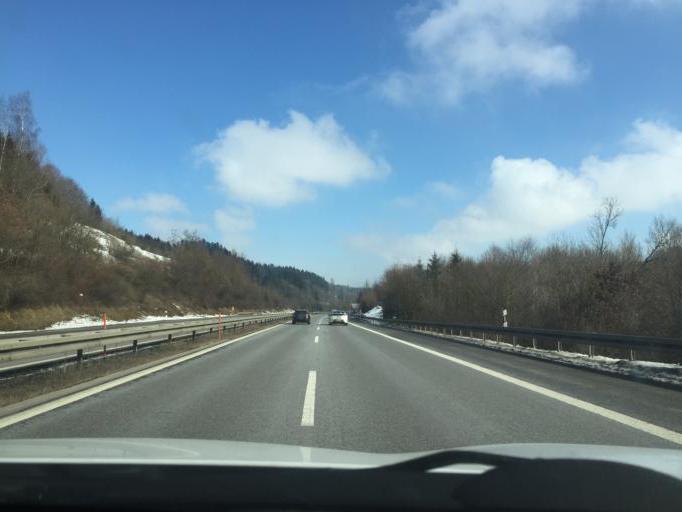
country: DE
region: Baden-Wuerttemberg
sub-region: Tuebingen Region
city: Wangen im Allgau
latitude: 47.7166
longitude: 9.8391
